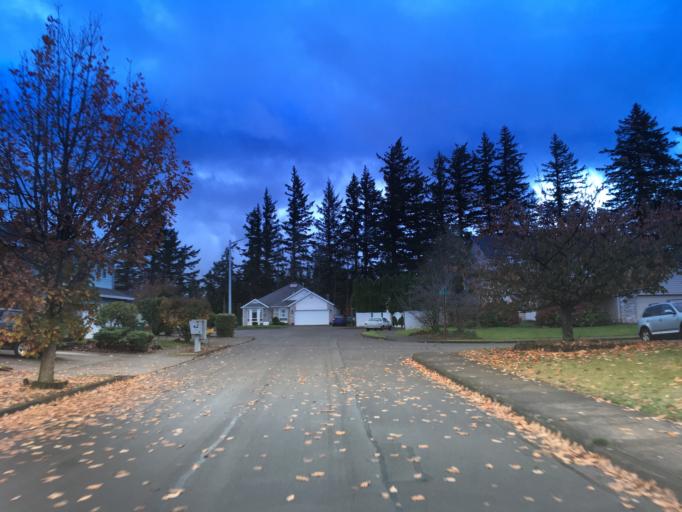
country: US
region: Oregon
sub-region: Multnomah County
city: Troutdale
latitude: 45.5202
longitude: -122.3935
